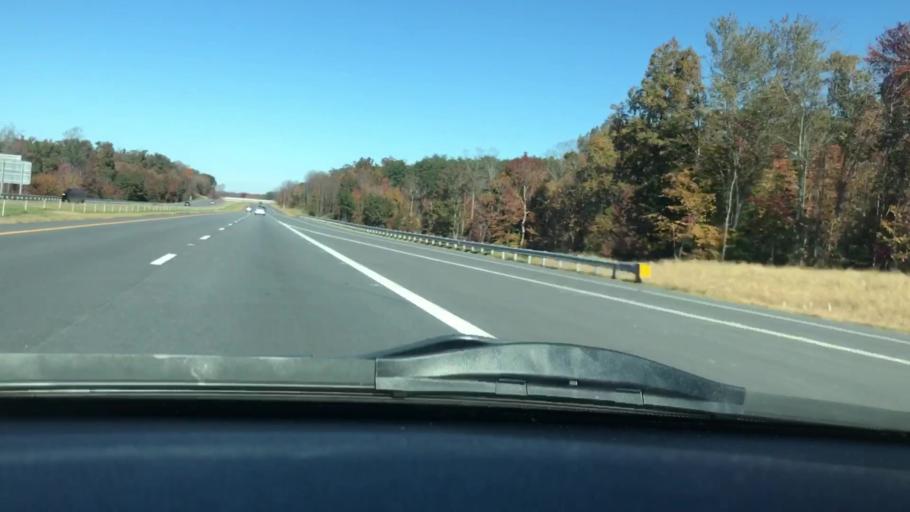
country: US
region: North Carolina
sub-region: Guilford County
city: Summerfield
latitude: 36.2058
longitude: -79.9251
